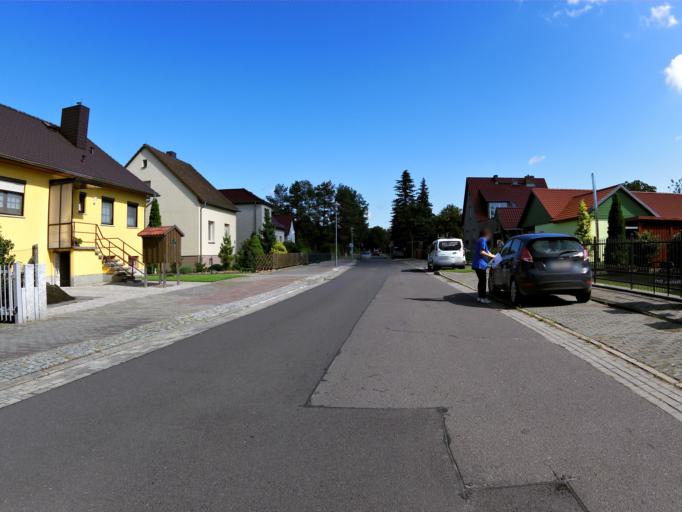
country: DE
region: Brandenburg
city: Storkow
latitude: 52.2493
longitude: 13.9416
